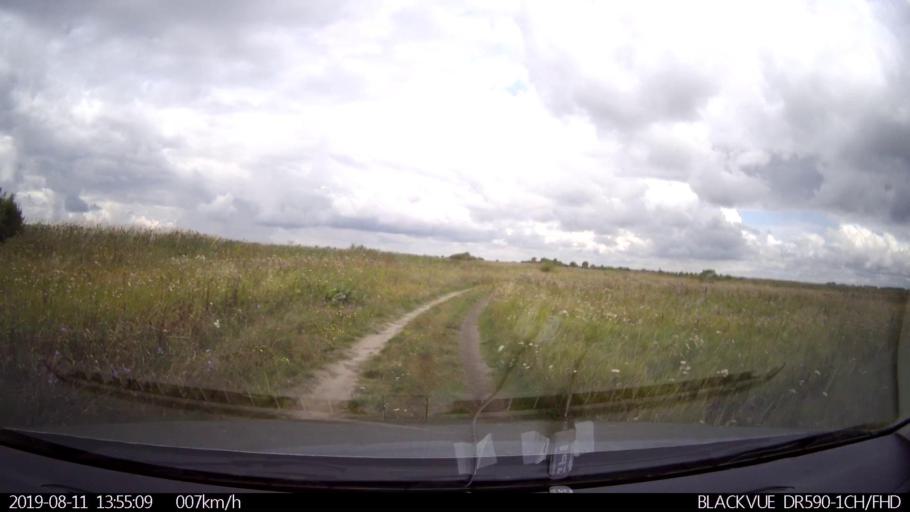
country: RU
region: Ulyanovsk
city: Ignatovka
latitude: 53.8454
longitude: 47.5866
